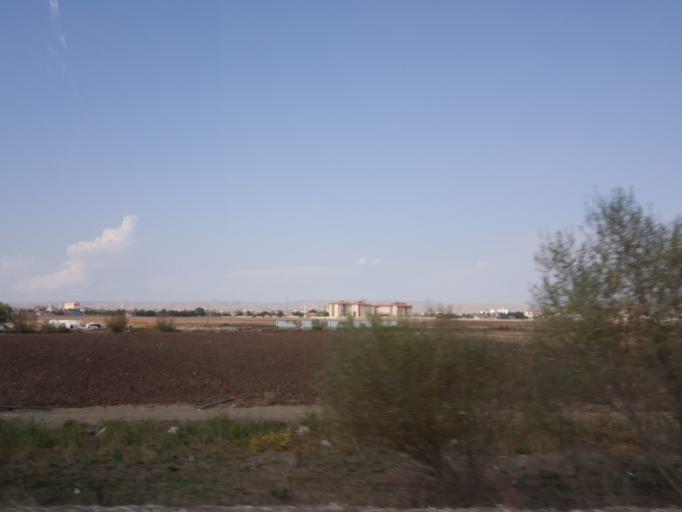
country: TR
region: Corum
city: Alaca
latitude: 40.1583
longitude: 34.8670
